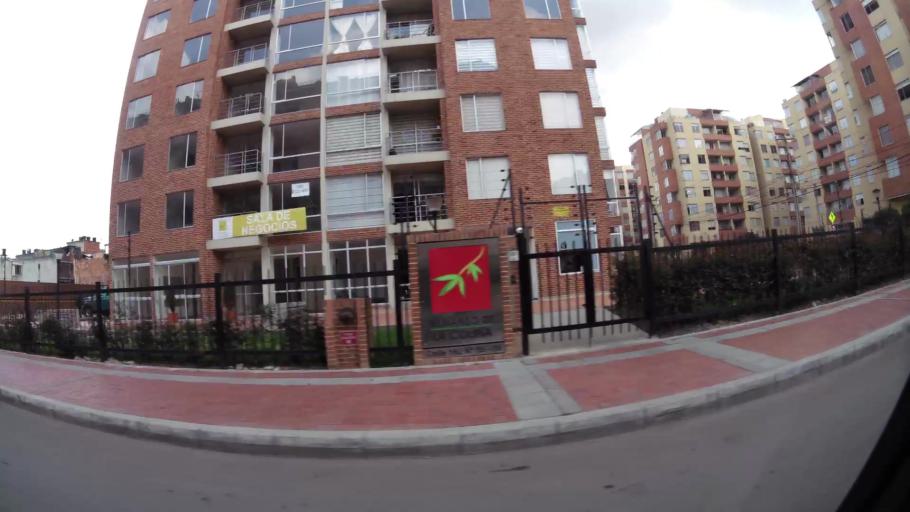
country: CO
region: Cundinamarca
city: Cota
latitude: 4.7449
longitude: -74.0576
